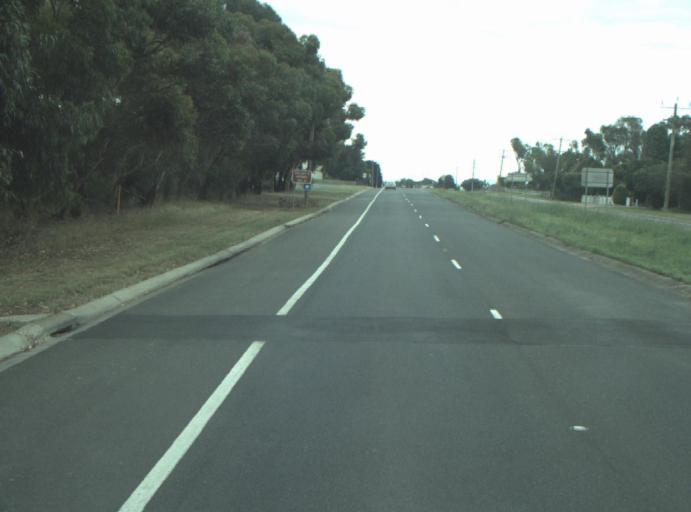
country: AU
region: Victoria
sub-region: Greater Geelong
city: Breakwater
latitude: -38.2184
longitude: 144.3379
